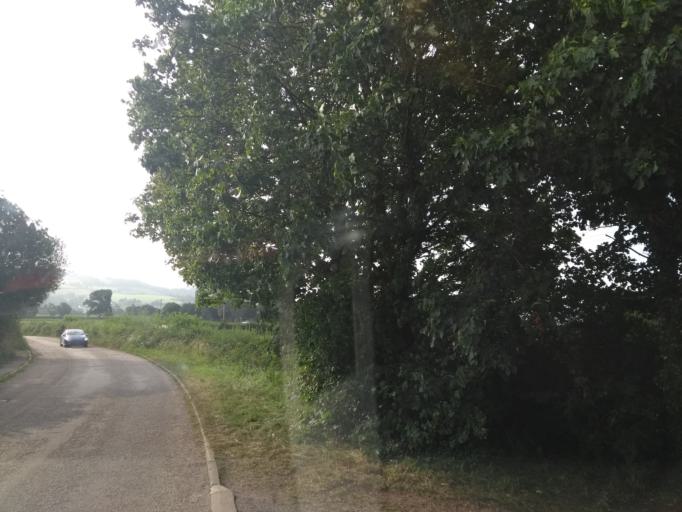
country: GB
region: England
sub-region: Devon
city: Colyton
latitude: 50.7529
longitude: -3.0468
